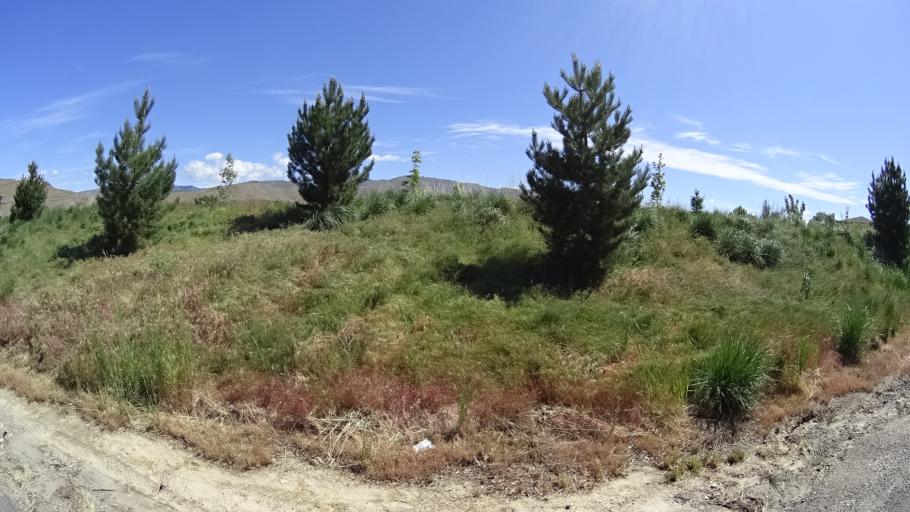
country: US
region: Idaho
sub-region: Ada County
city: Boise
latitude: 43.5638
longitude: -116.1330
